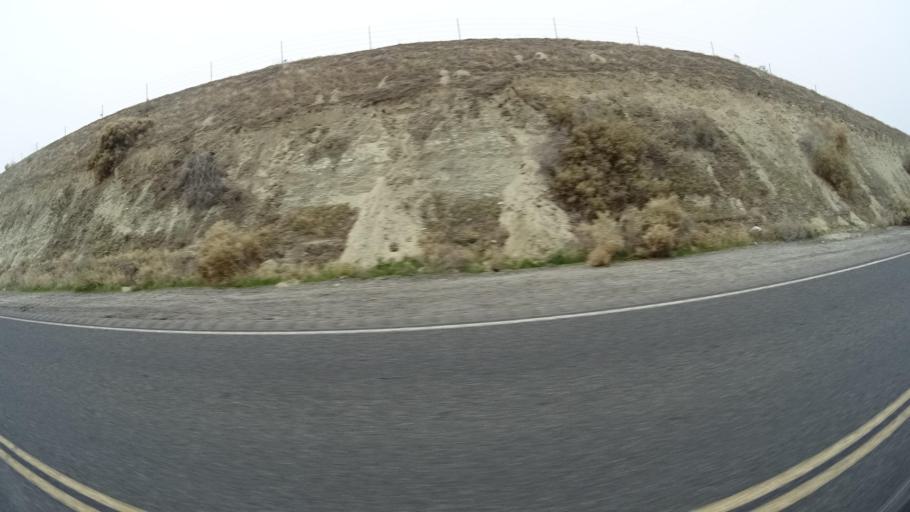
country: US
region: California
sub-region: Kern County
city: Buttonwillow
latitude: 35.3063
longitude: -119.4671
